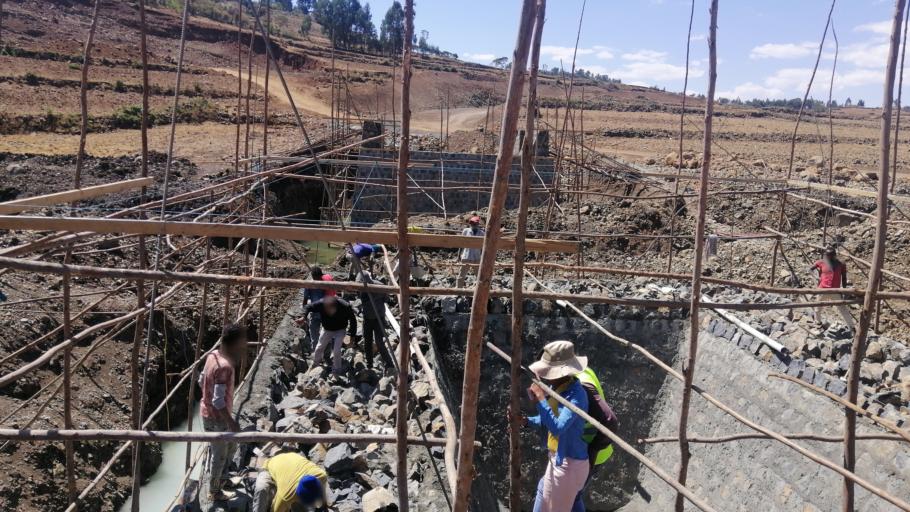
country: ET
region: Amhara
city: Debre Tabor
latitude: 11.4527
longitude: 38.1513
